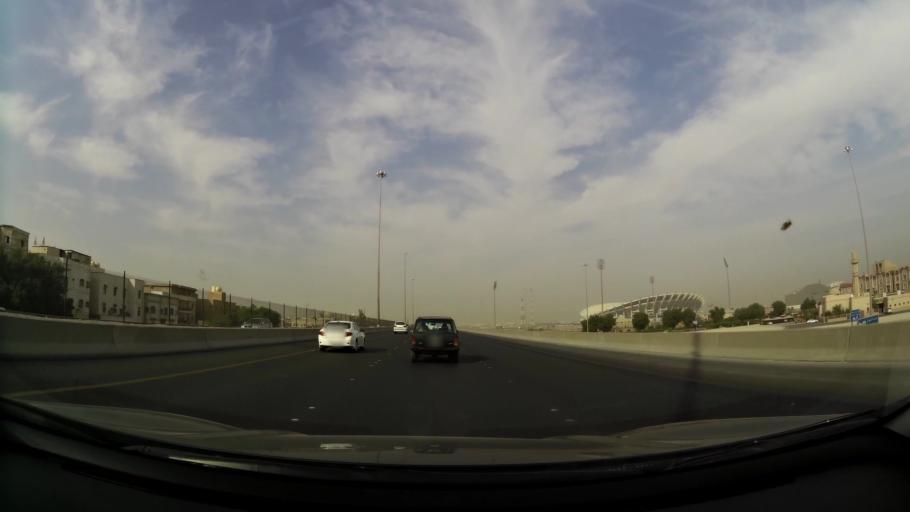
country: KW
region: Al Asimah
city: Ar Rabiyah
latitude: 29.2671
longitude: 47.9277
